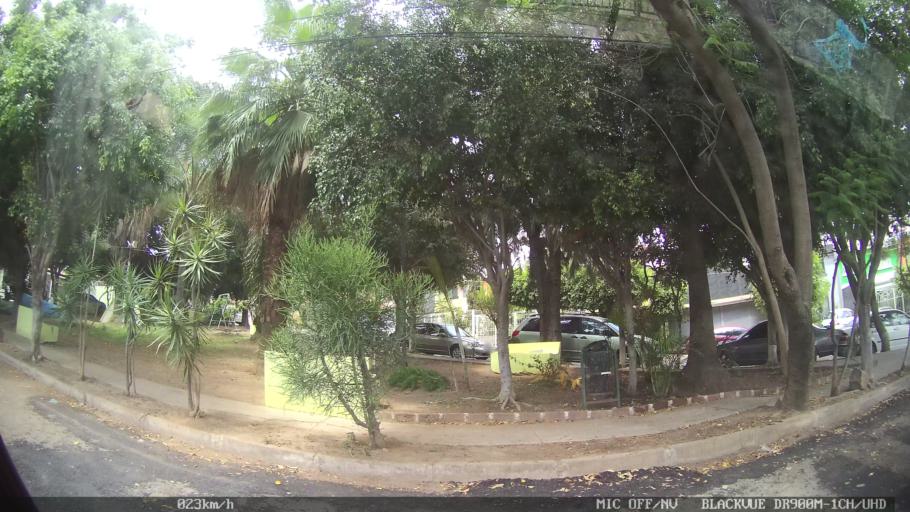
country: MX
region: Jalisco
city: Tonala
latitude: 20.6283
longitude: -103.2511
